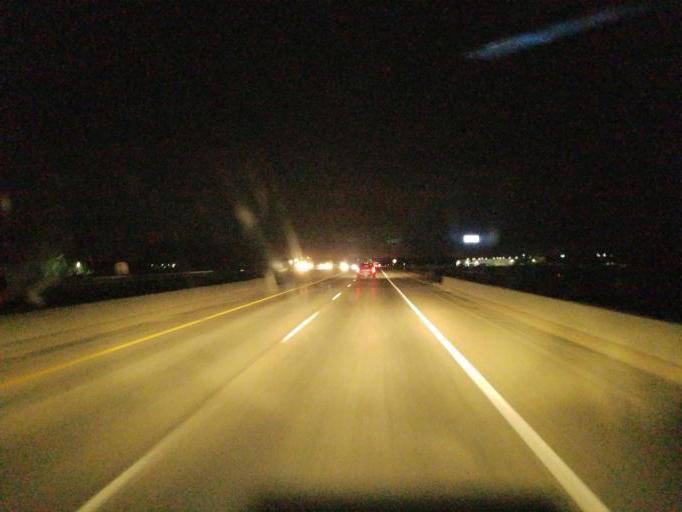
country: US
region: Iowa
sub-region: Dallas County
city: De Soto
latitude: 41.5401
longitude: -94.0128
